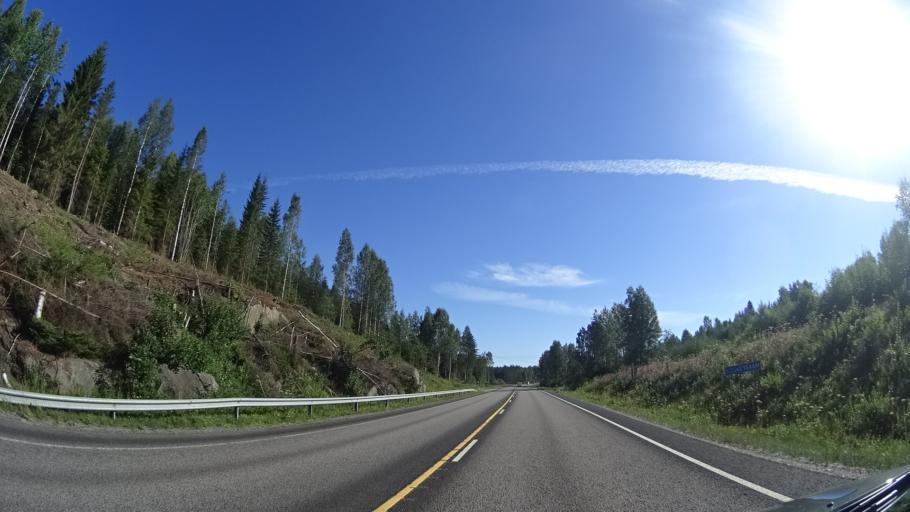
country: FI
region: Central Finland
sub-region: Jyvaeskylae
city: Petaejaevesi
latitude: 62.2640
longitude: 25.2791
